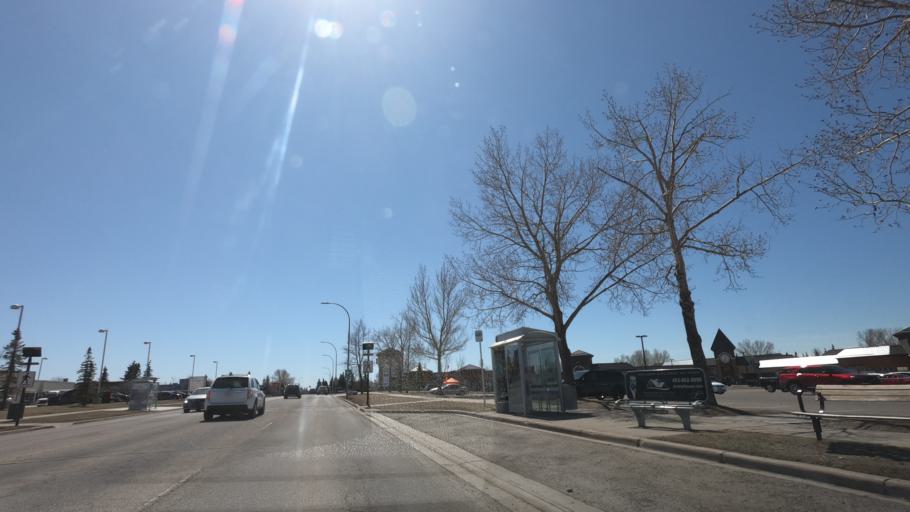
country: CA
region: Alberta
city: Airdrie
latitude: 51.2879
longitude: -114.0135
